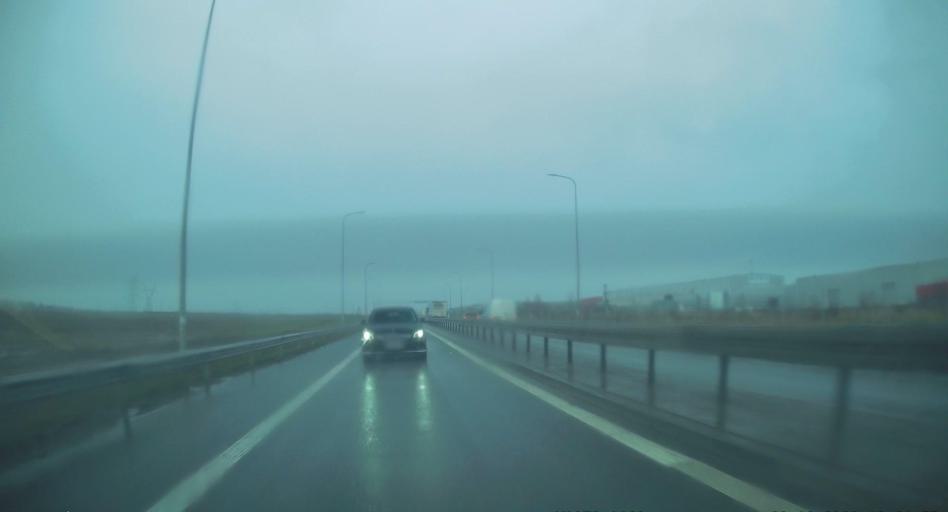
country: PL
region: Lodz Voivodeship
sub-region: Powiat radomszczanski
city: Radomsko
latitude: 51.0868
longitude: 19.3770
